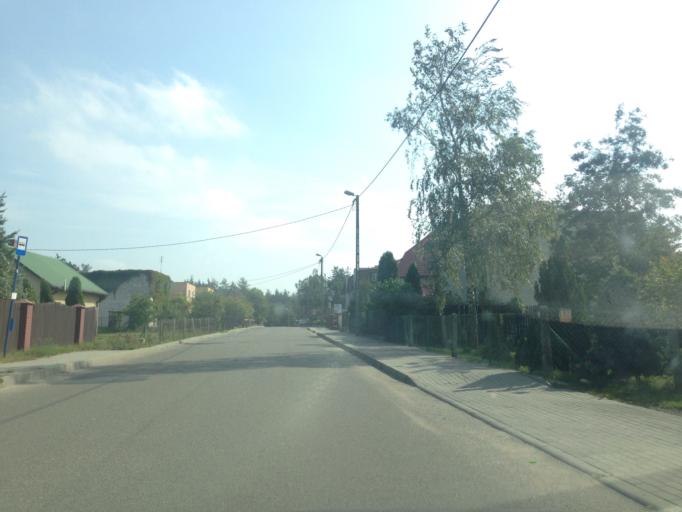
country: PL
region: Kujawsko-Pomorskie
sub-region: Powiat brodnicki
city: Brodnica
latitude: 53.2727
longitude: 19.4172
